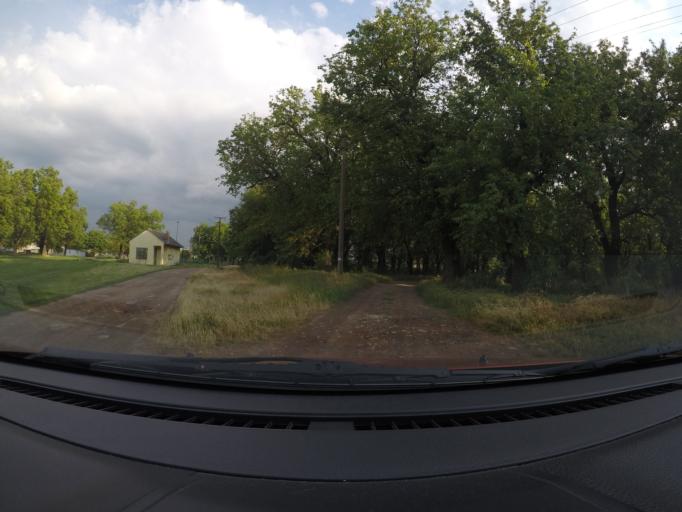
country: RS
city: Debeljaca
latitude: 45.0642
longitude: 20.6034
